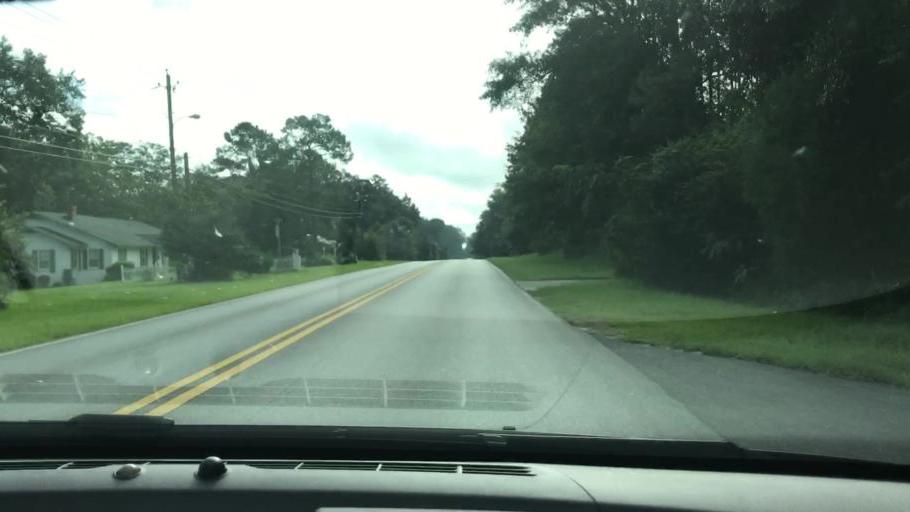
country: US
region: Florida
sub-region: Jackson County
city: Marianna
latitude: 30.7690
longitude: -85.2411
